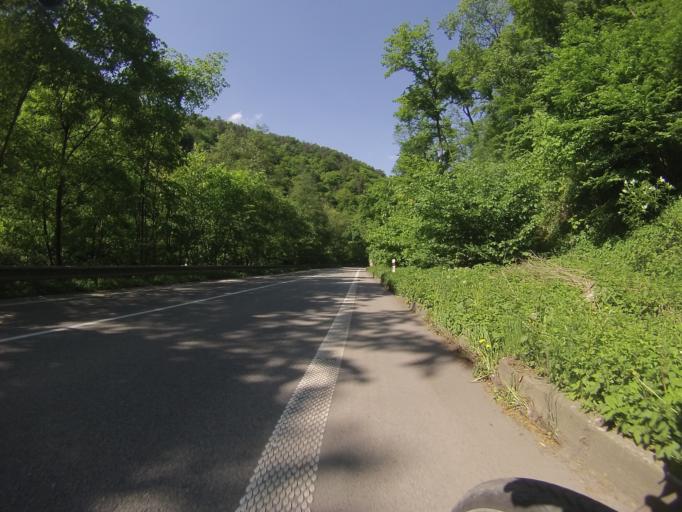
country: CZ
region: South Moravian
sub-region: Okres Blansko
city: Blansko
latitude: 49.3340
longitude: 16.6453
